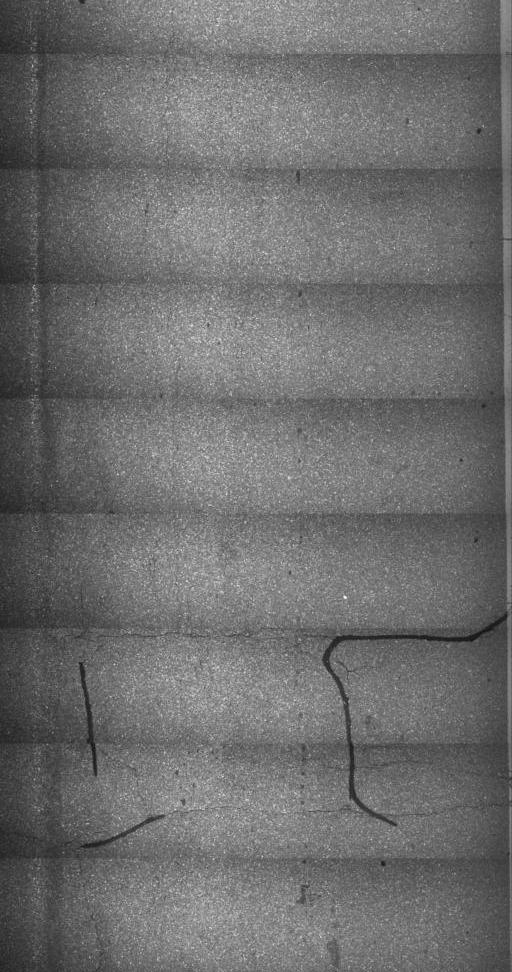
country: US
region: Vermont
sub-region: Windsor County
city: Springfield
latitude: 43.3092
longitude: -72.4971
